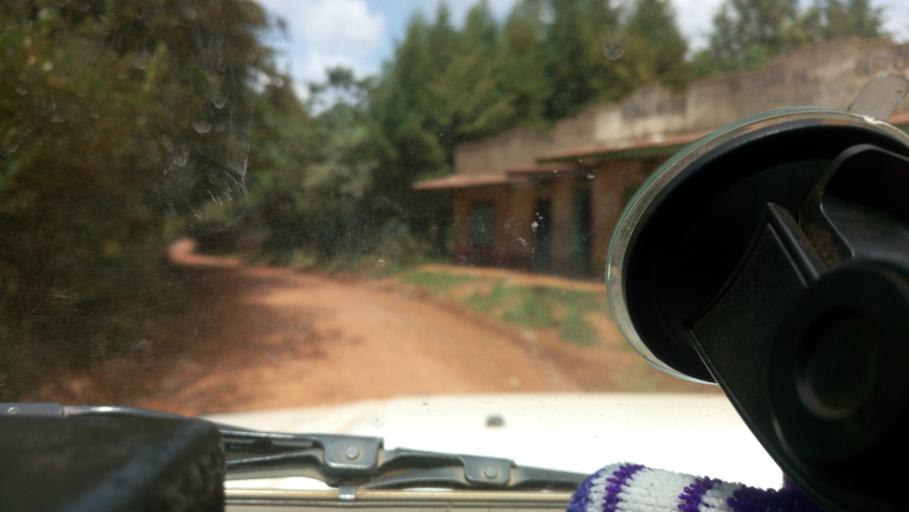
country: KE
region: Kericho
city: Litein
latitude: -0.6138
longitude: 35.1311
